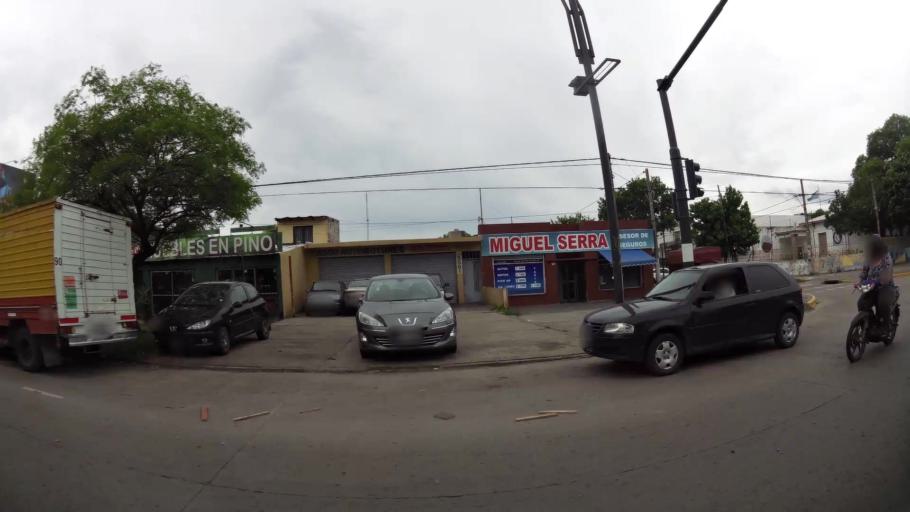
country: AR
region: Santa Fe
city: Gobernador Galvez
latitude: -33.0023
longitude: -60.6649
